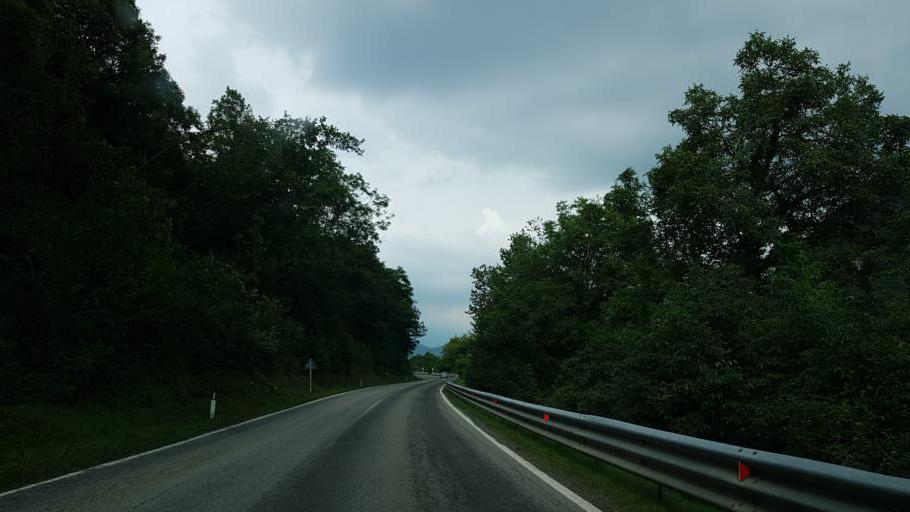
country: IT
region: Piedmont
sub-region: Provincia di Cuneo
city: Moiola
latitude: 44.3243
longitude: 7.3939
